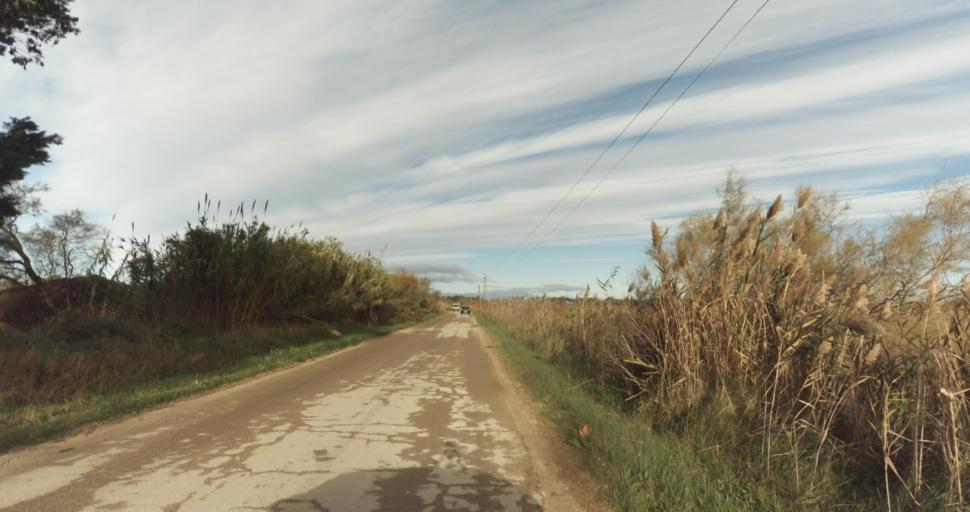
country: FR
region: Languedoc-Roussillon
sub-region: Departement du Gard
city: Aigues-Mortes
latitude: 43.5553
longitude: 4.2226
